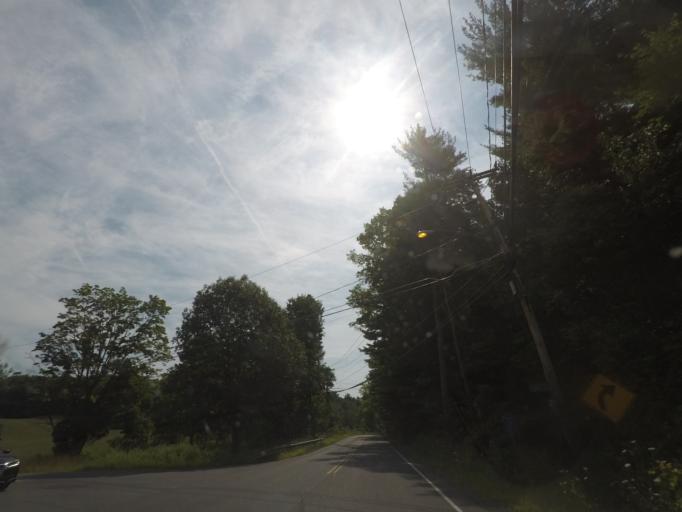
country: US
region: New York
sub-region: Rensselaer County
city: Wynantskill
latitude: 42.7041
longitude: -73.6128
